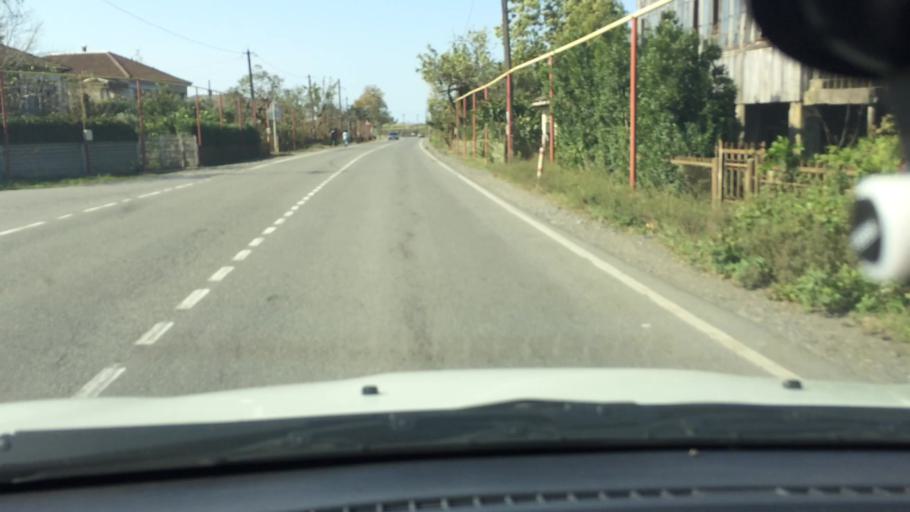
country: GE
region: Guria
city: Urek'i
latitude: 42.0418
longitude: 41.8103
